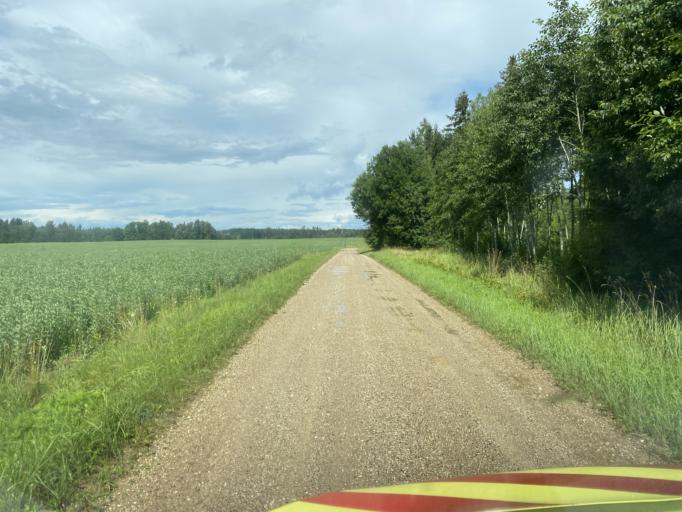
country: EE
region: Valgamaa
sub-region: Torva linn
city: Torva
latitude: 58.1022
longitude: 26.0030
